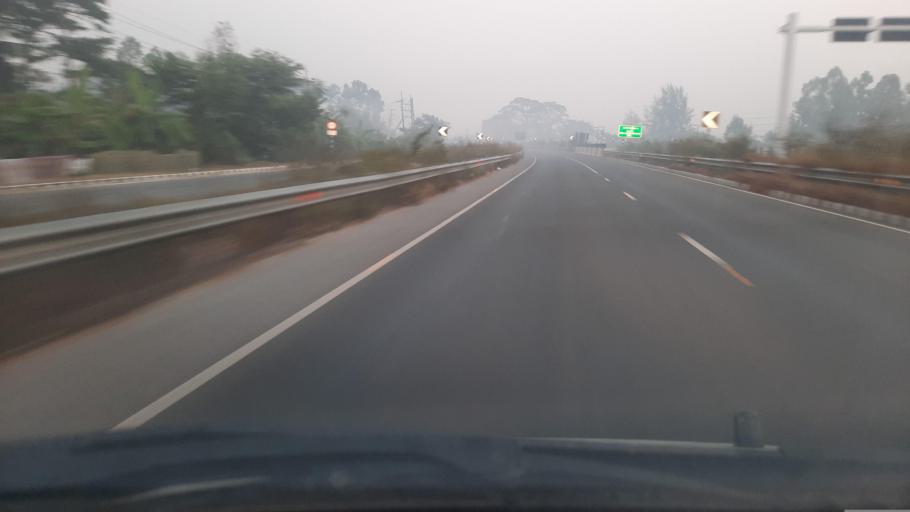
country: BD
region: Dhaka
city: Dohar
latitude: 23.5470
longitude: 90.2989
